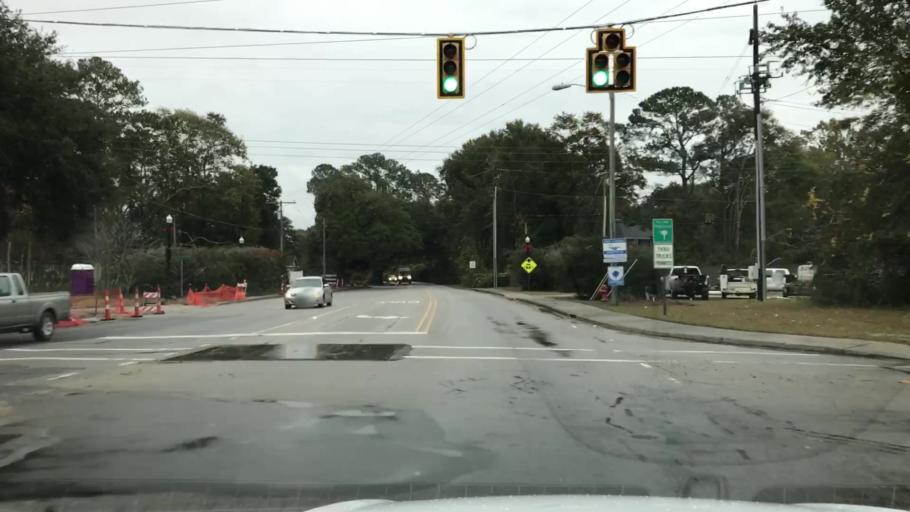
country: US
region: South Carolina
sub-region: Charleston County
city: Mount Pleasant
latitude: 32.8414
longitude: -79.8462
